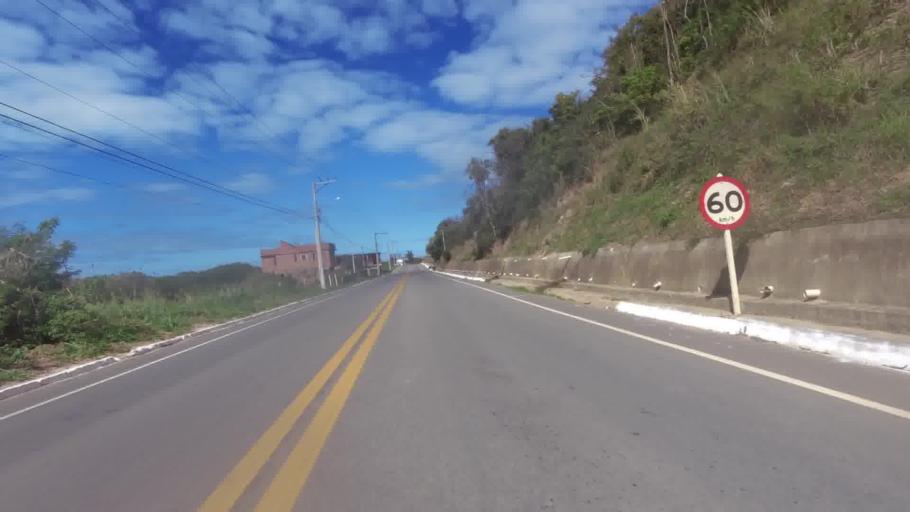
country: BR
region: Espirito Santo
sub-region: Marataizes
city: Marataizes
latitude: -21.0984
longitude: -40.8488
